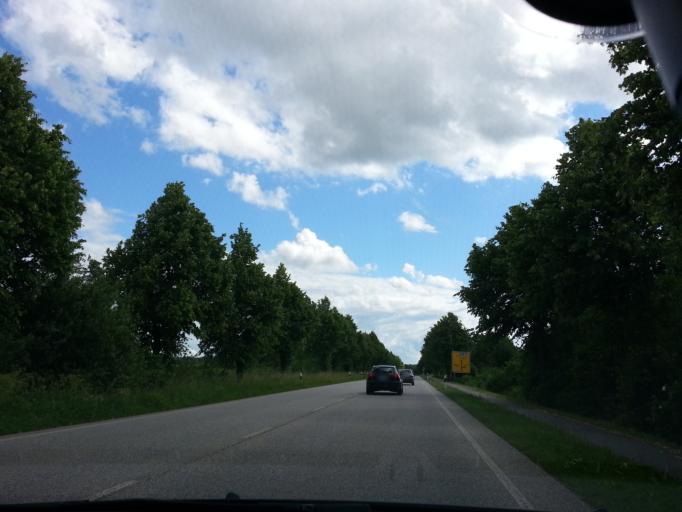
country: DE
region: Schleswig-Holstein
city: Harmsdorf
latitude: 53.6908
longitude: 10.7297
